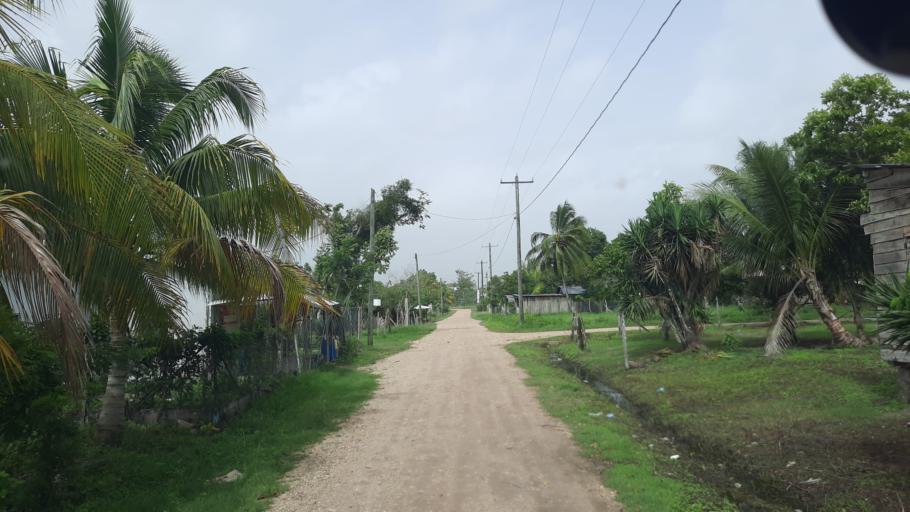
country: BZ
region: Cayo
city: Valley of Peace
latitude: 17.2512
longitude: -88.9406
